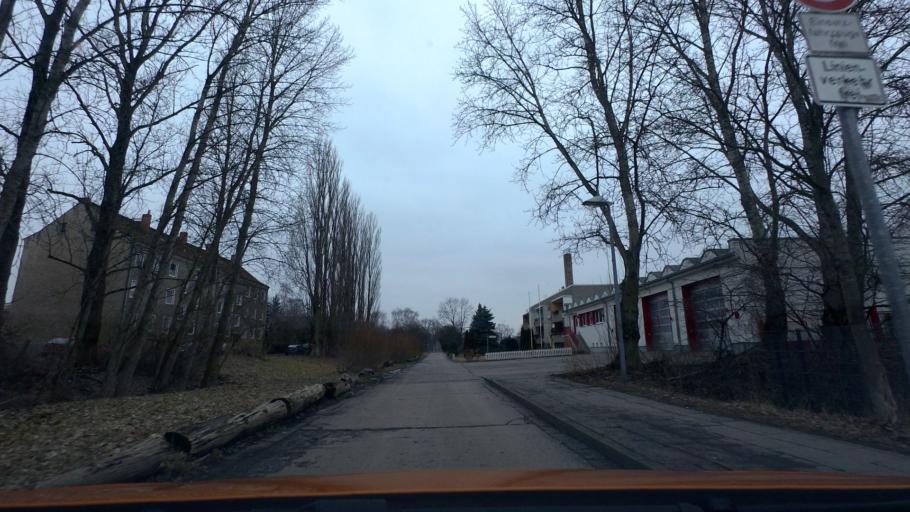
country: DE
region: Berlin
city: Falkenberg
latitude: 52.5692
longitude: 13.5471
